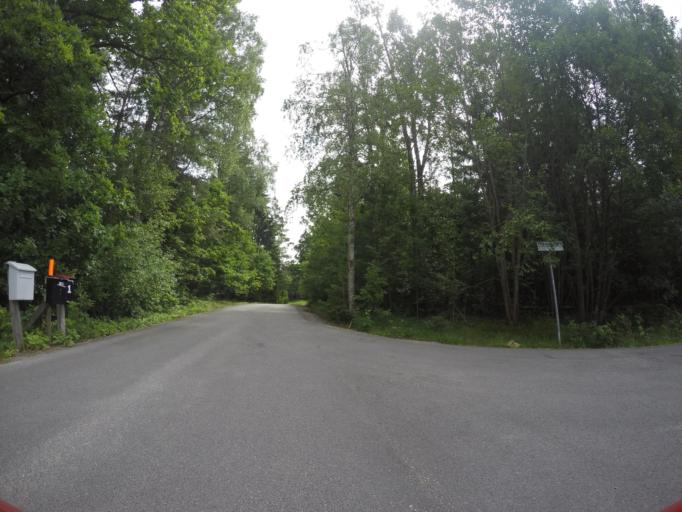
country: SE
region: Vaestra Goetaland
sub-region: Trollhattan
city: Trollhattan
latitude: 58.2322
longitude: 12.3158
